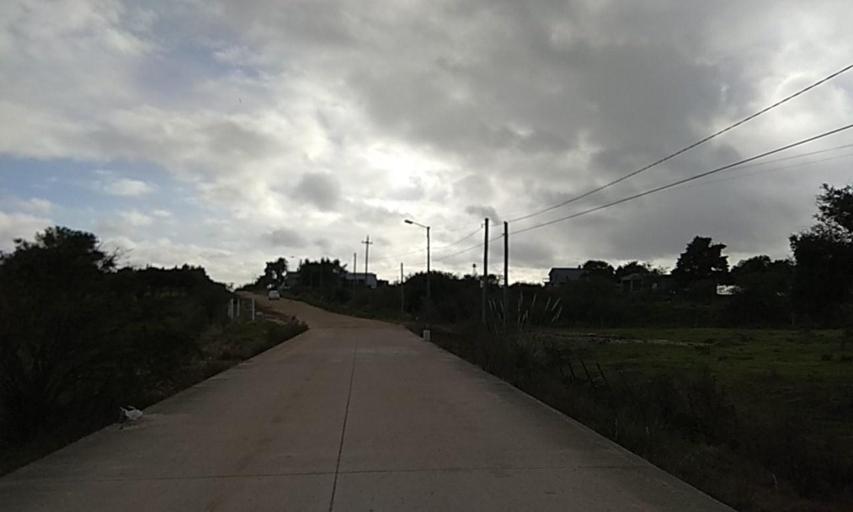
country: UY
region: Florida
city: Florida
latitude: -34.0705
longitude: -56.1954
